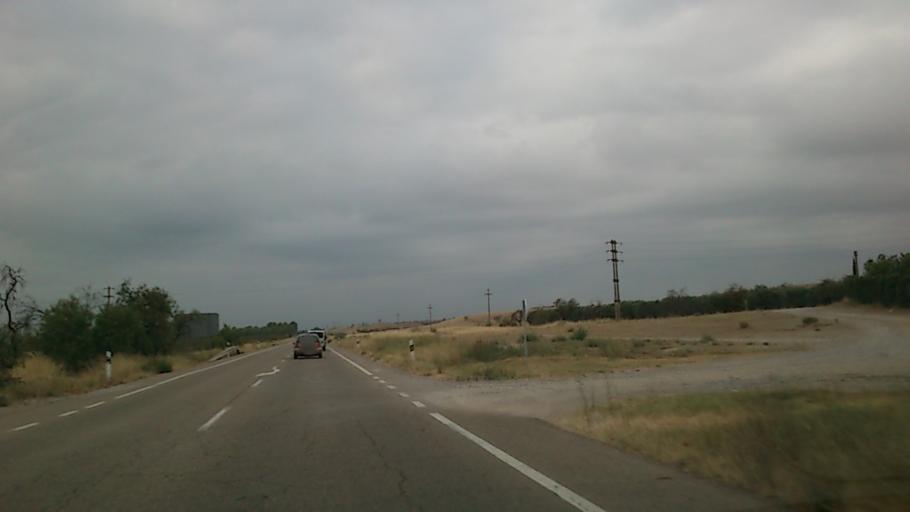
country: ES
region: Aragon
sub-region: Provincia de Zaragoza
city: Villanueva de Gallego
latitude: 41.7958
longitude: -0.8115
